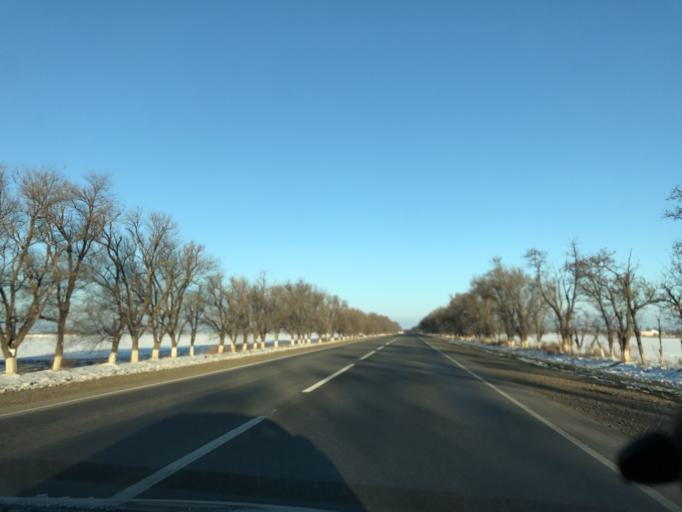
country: RU
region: Stavropol'skiy
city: Bezopasnoye
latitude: 45.6197
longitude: 41.9380
